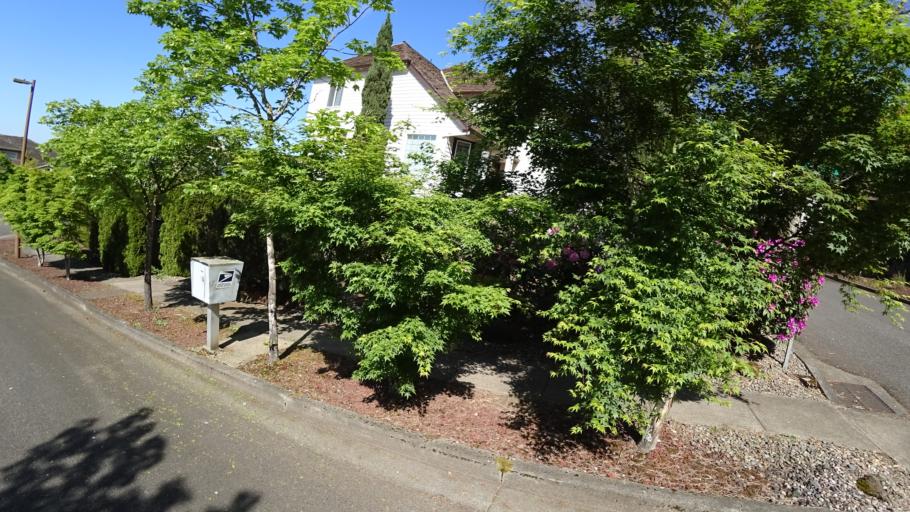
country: US
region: Oregon
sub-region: Washington County
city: Aloha
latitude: 45.4741
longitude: -122.8475
